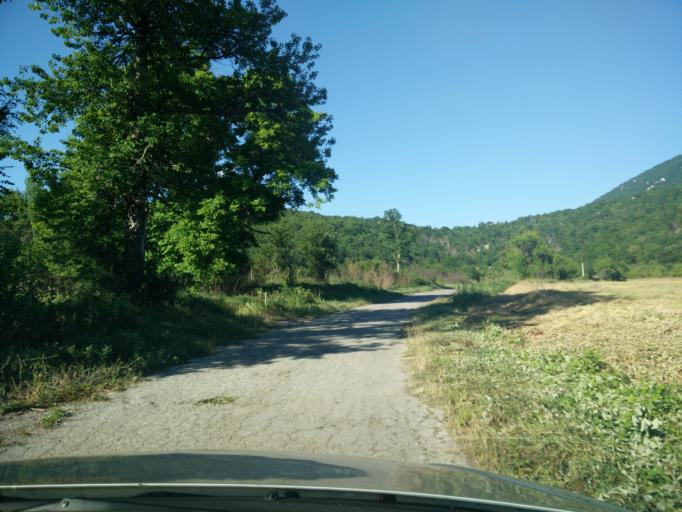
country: HR
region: Zadarska
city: Gracac
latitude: 44.4518
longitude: 15.6743
